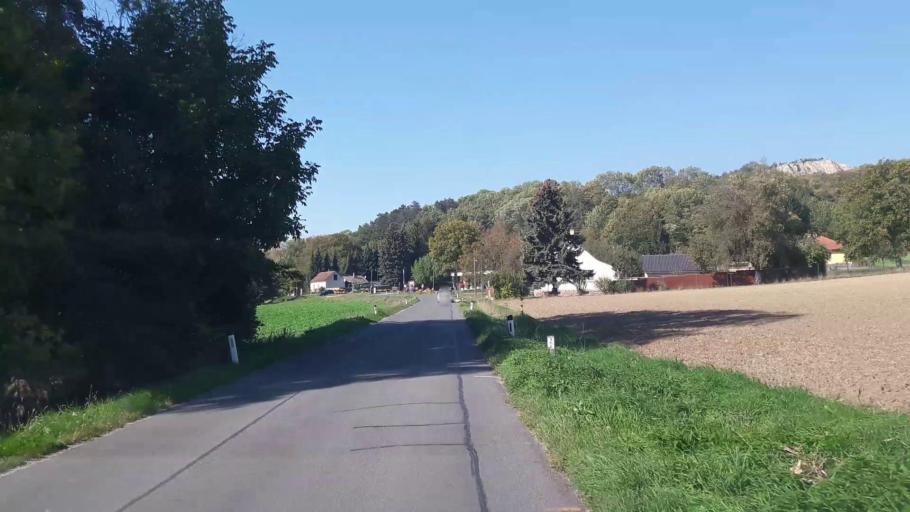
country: AT
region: Lower Austria
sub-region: Politischer Bezirk Korneuburg
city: Ernstbrunn
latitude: 48.5398
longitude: 16.3597
